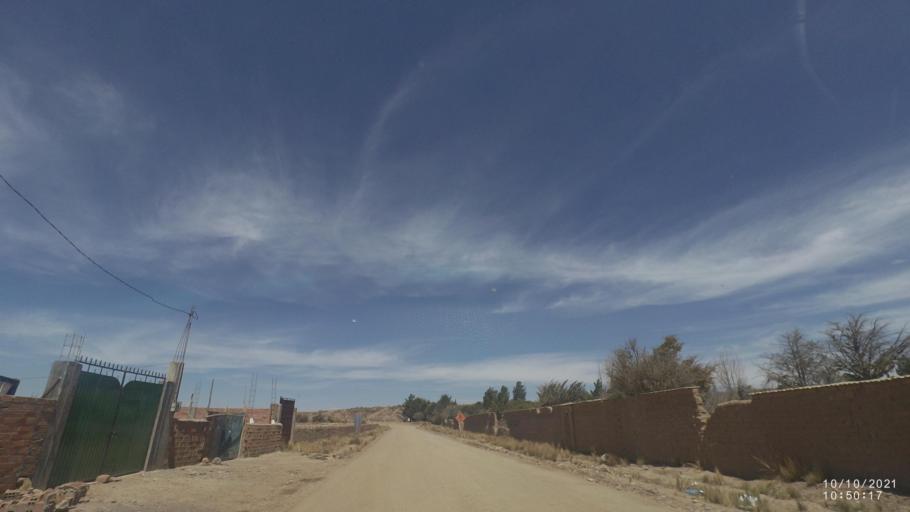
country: BO
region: La Paz
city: Colquiri
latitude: -17.6483
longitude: -67.2145
